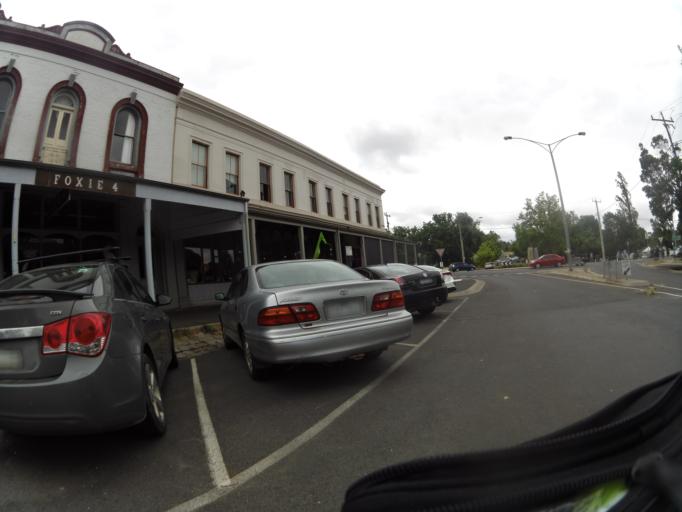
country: AU
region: Victoria
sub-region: Mount Alexander
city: Castlemaine
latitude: -37.0665
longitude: 144.2190
